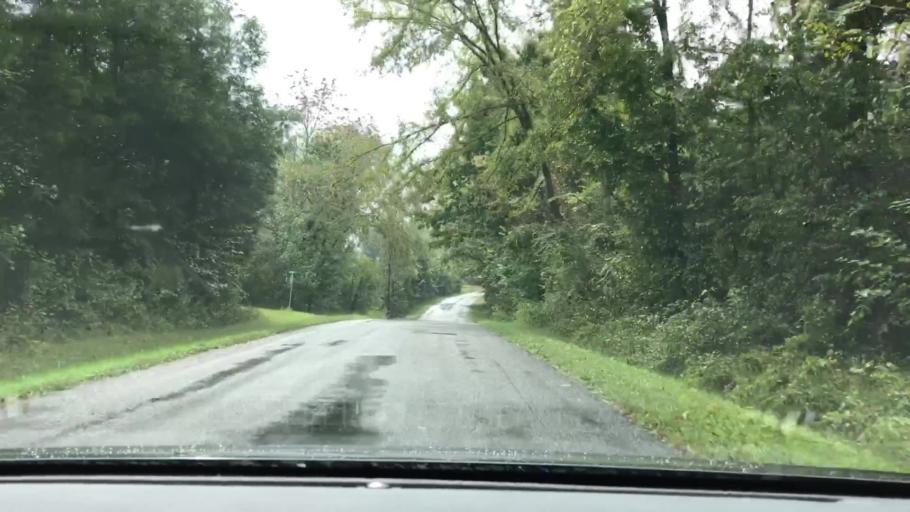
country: US
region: Tennessee
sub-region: Macon County
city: Red Boiling Springs
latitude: 36.5959
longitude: -85.7758
